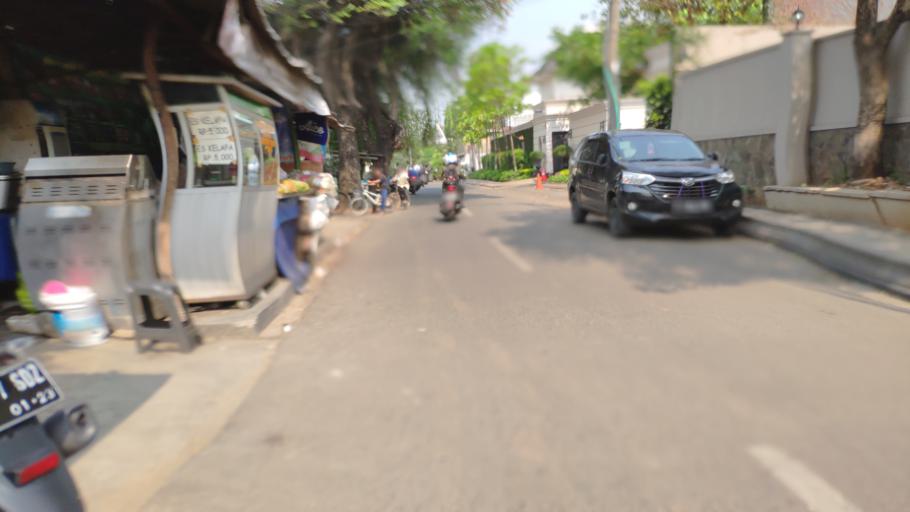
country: ID
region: Jakarta Raya
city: Jakarta
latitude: -6.2544
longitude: 106.8211
